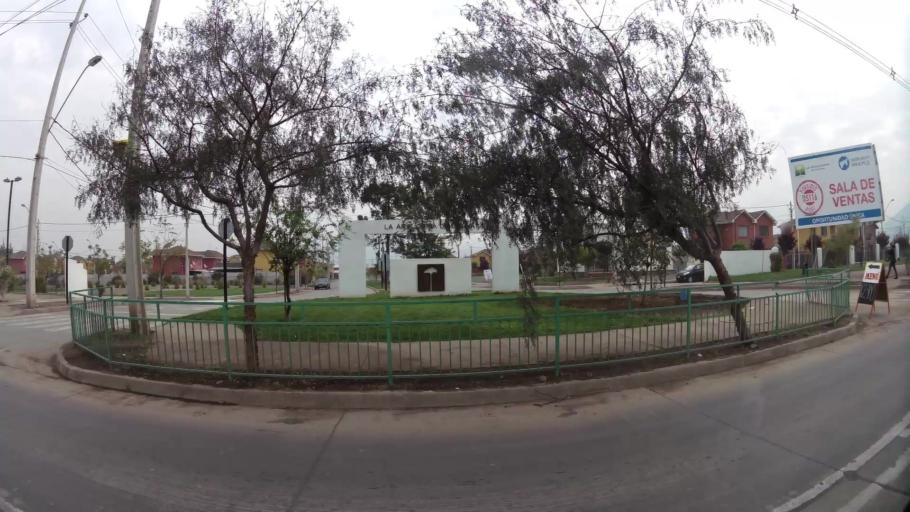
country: CL
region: Santiago Metropolitan
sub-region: Provincia de Chacabuco
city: Chicureo Abajo
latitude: -33.1934
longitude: -70.6777
